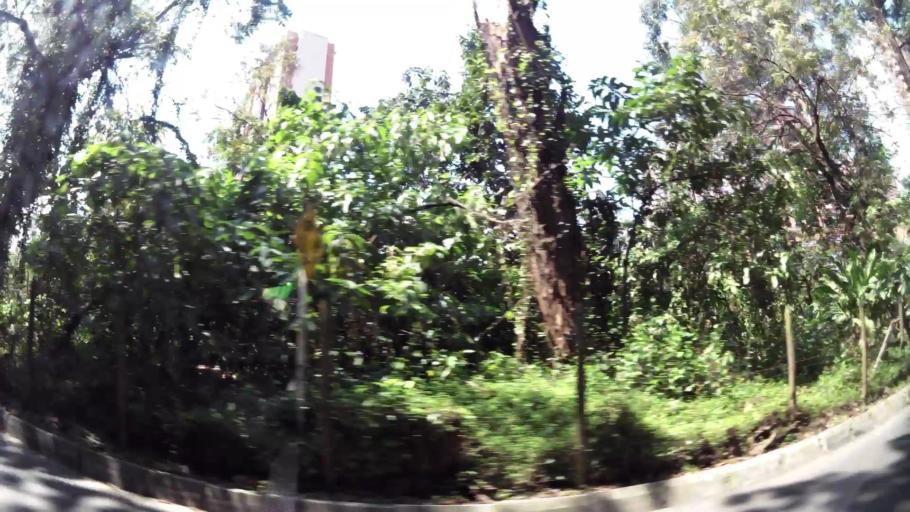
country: CO
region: Antioquia
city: Itagui
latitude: 6.2163
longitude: -75.6044
